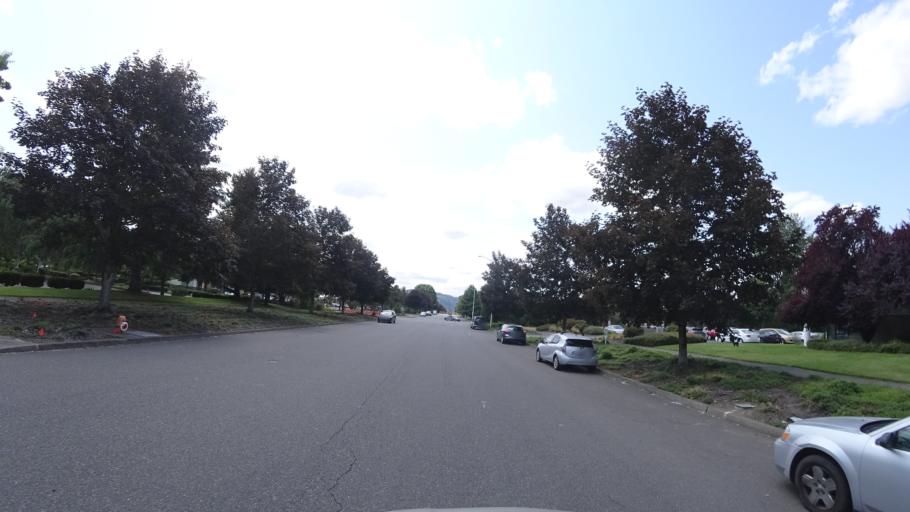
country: US
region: Washington
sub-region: Clark County
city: Lake Shore
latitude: 45.6239
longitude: -122.7703
